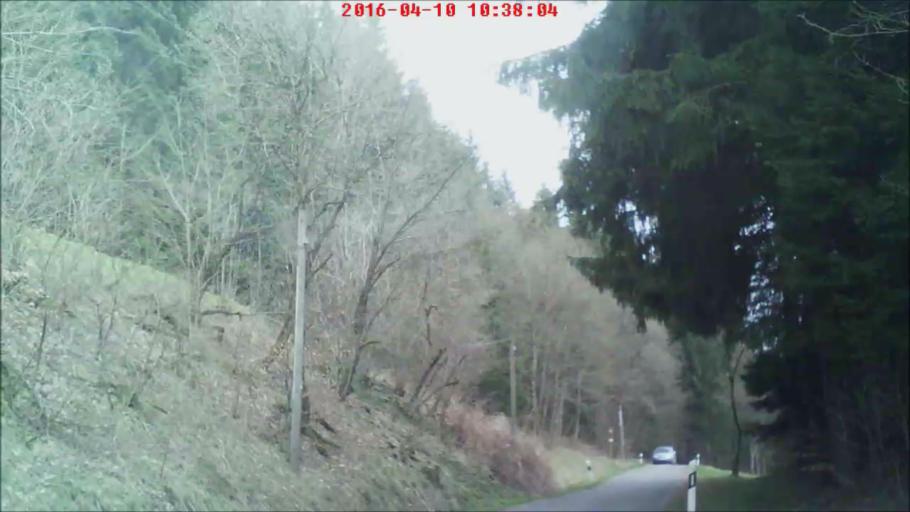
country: DE
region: Thuringia
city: Stutzerbach
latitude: 50.6233
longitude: 10.8555
